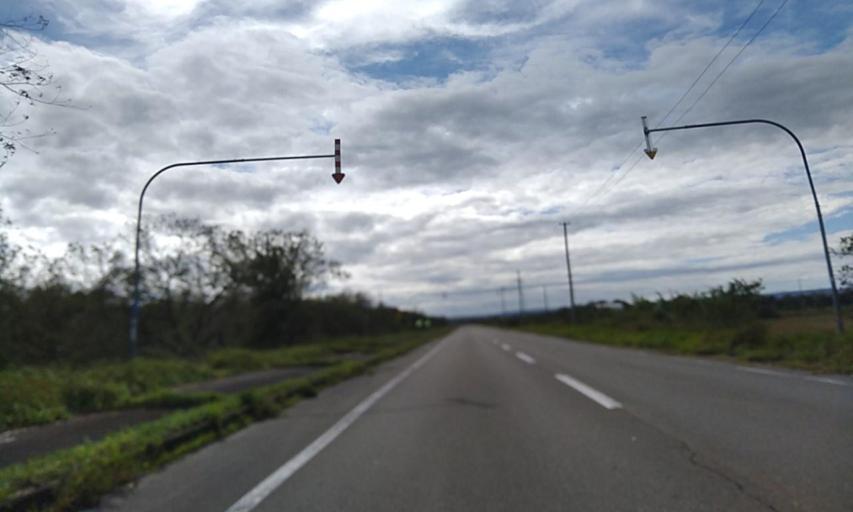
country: JP
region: Hokkaido
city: Obihiro
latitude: 42.7238
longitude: 143.6644
